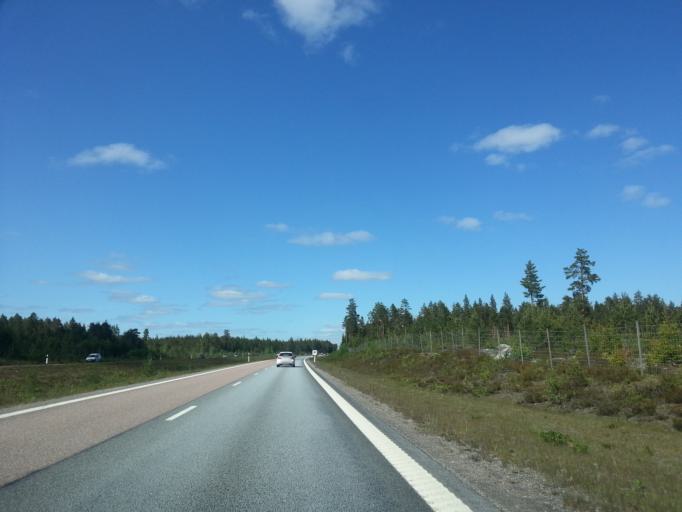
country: SE
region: Gaevleborg
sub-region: Soderhamns Kommun
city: Soderhamn
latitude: 61.3835
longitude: 16.9929
